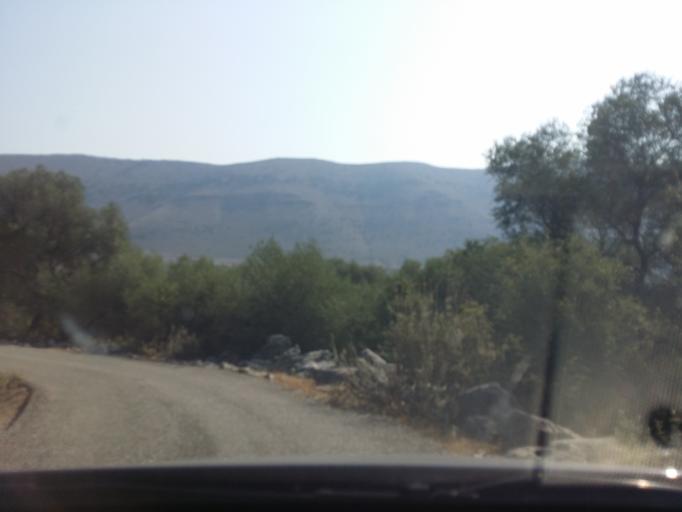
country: GR
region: West Greece
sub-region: Nomos Aitolias kai Akarnanias
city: Stanos
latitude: 38.8243
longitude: 21.1664
